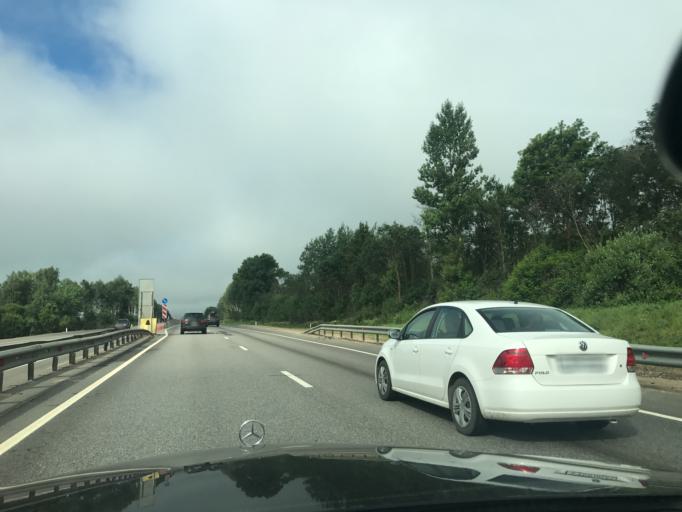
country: RU
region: Smolensk
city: Vyaz'ma
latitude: 55.2590
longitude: 34.3679
